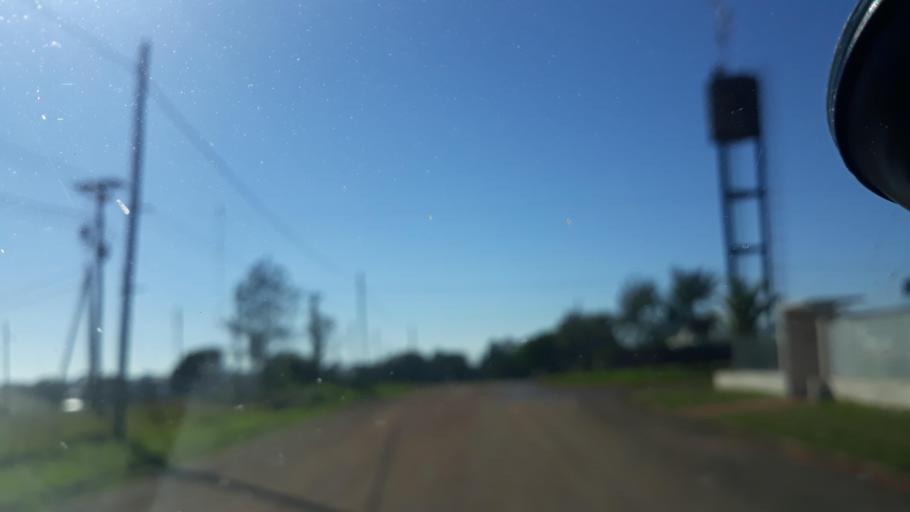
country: AR
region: Misiones
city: Bernardo de Irigoyen
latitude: -26.2631
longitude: -53.6499
